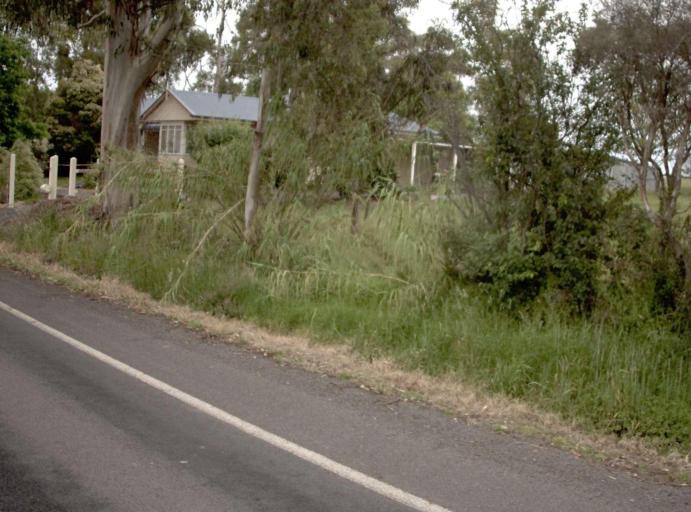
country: AU
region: Victoria
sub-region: Baw Baw
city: Warragul
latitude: -38.5003
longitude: 145.9519
